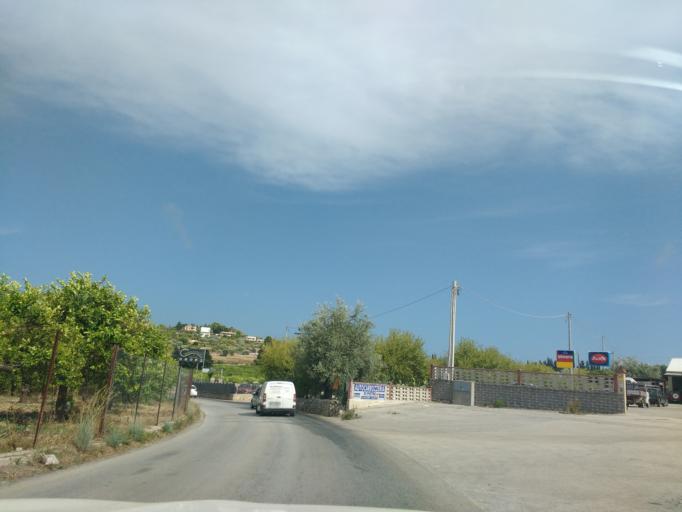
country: IT
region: Sicily
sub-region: Provincia di Siracusa
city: Noto
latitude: 36.8762
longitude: 15.0778
